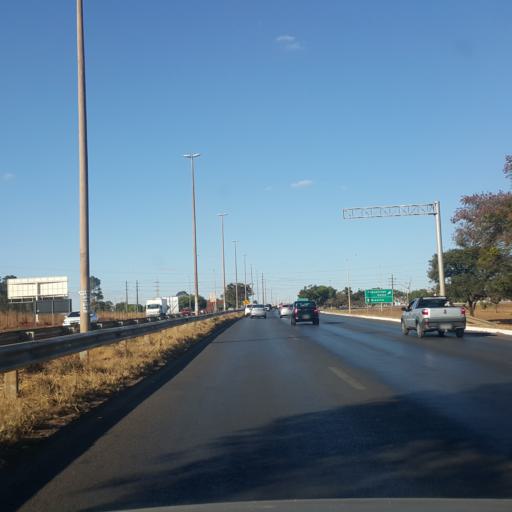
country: BR
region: Federal District
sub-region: Brasilia
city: Brasilia
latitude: -15.7932
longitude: -48.0575
